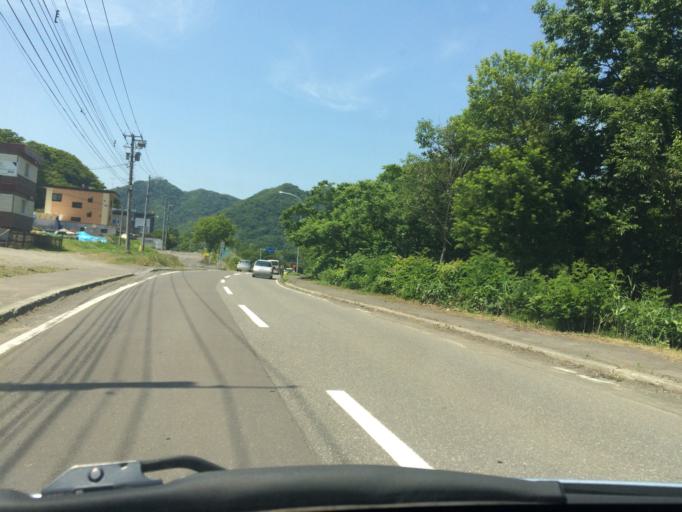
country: JP
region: Hokkaido
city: Sapporo
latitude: 42.9647
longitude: 141.2741
